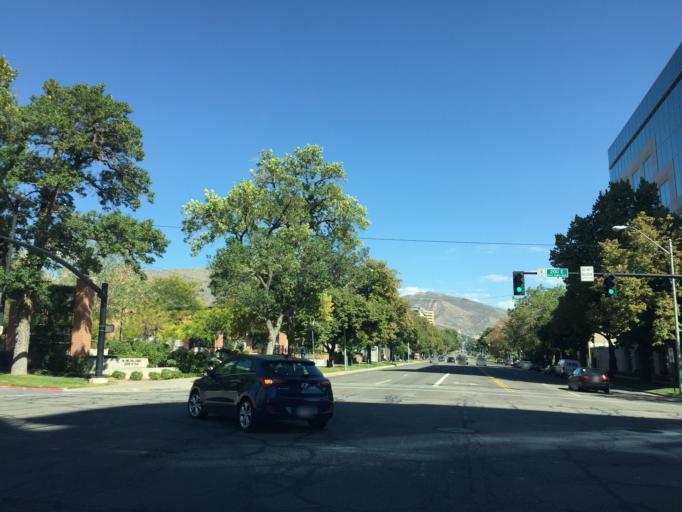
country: US
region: Utah
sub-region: Salt Lake County
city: Salt Lake City
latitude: 40.7672
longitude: -111.8856
